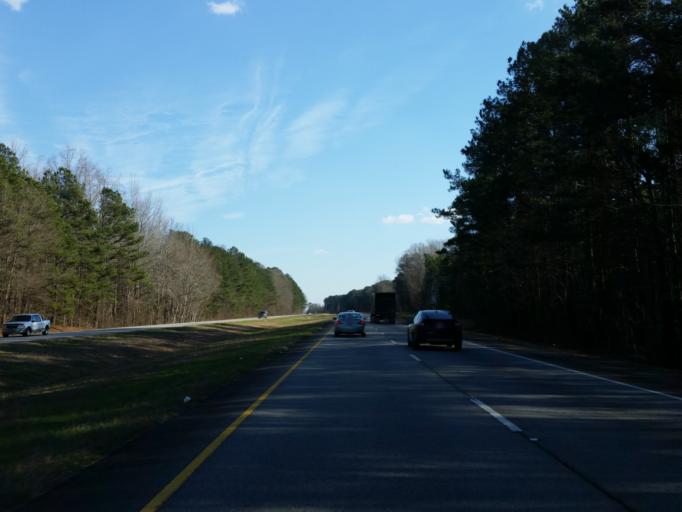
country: US
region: Georgia
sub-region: Lamar County
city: Barnesville
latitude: 33.1203
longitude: -84.2148
